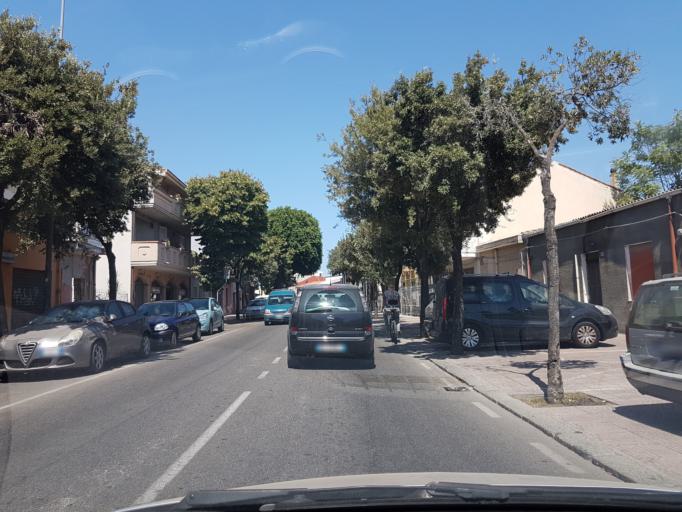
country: IT
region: Sardinia
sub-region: Provincia di Oristano
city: Oristano
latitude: 39.8979
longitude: 8.5946
